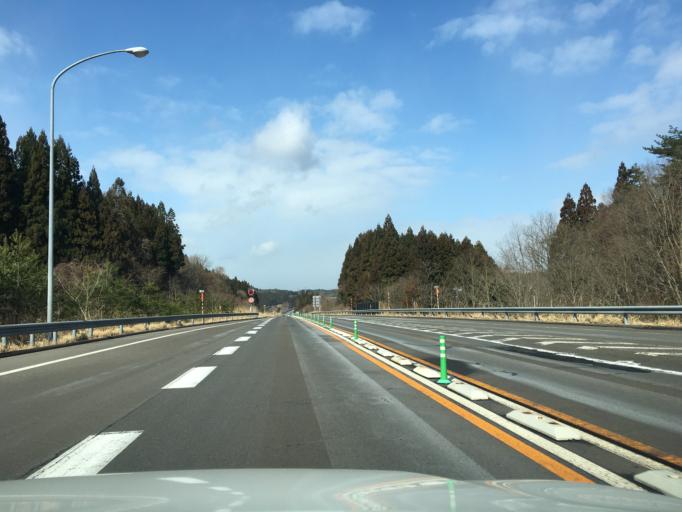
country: JP
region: Akita
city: Akita
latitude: 39.7508
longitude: 140.1490
